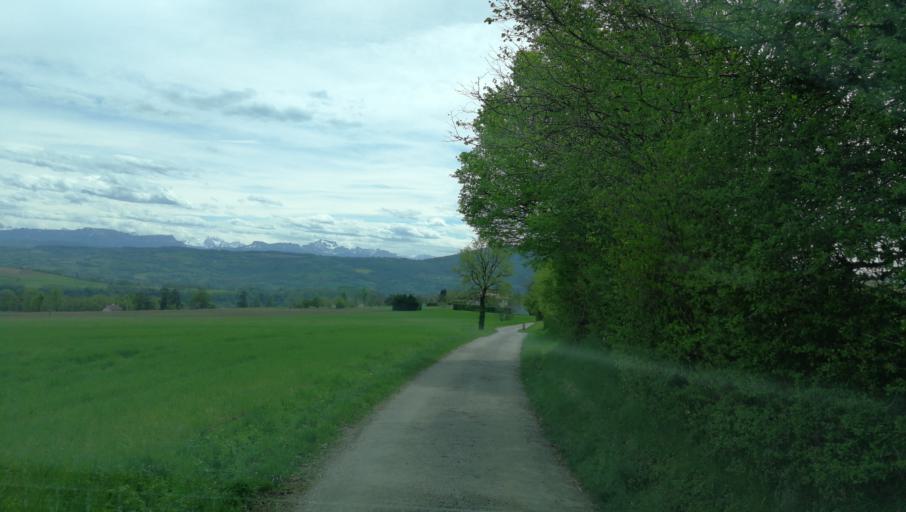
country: FR
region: Rhone-Alpes
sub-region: Departement de l'Ain
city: Bellegarde-sur-Valserine
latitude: 46.0104
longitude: 5.7798
